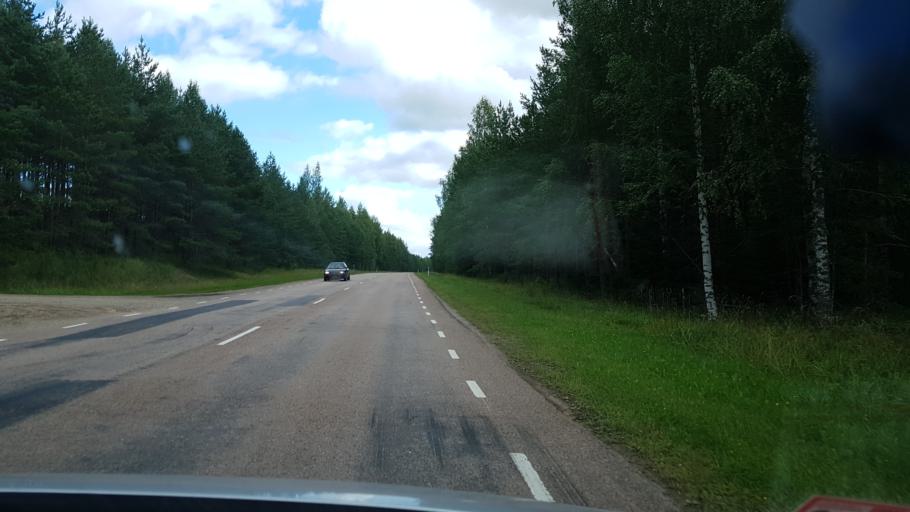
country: EE
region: Vorumaa
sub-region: Voru linn
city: Voru
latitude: 57.7691
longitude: 26.8573
